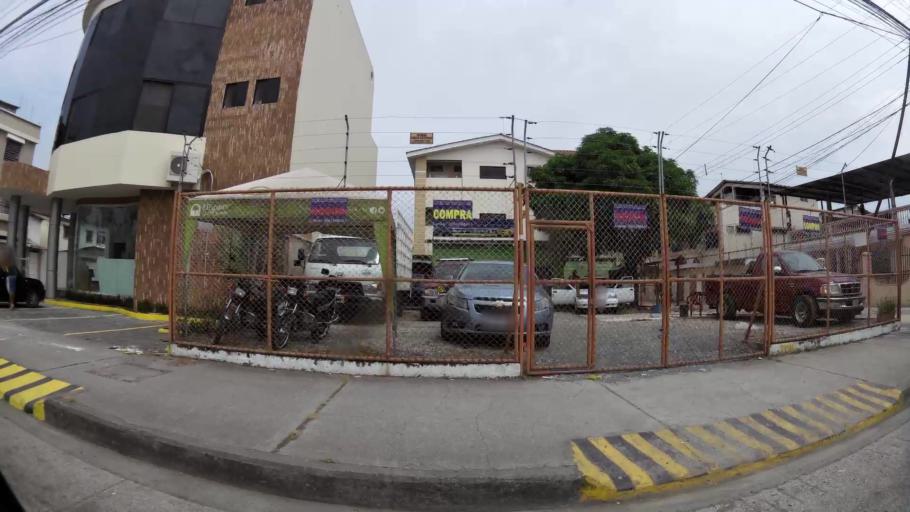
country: EC
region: Guayas
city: Eloy Alfaro
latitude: -2.1501
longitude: -79.8940
